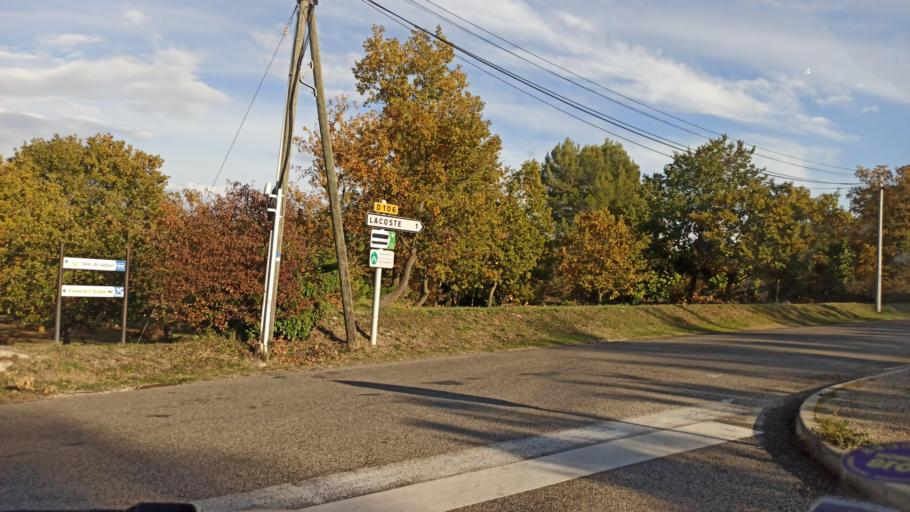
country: FR
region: Provence-Alpes-Cote d'Azur
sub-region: Departement du Vaucluse
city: Goult
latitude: 43.8367
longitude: 5.2691
